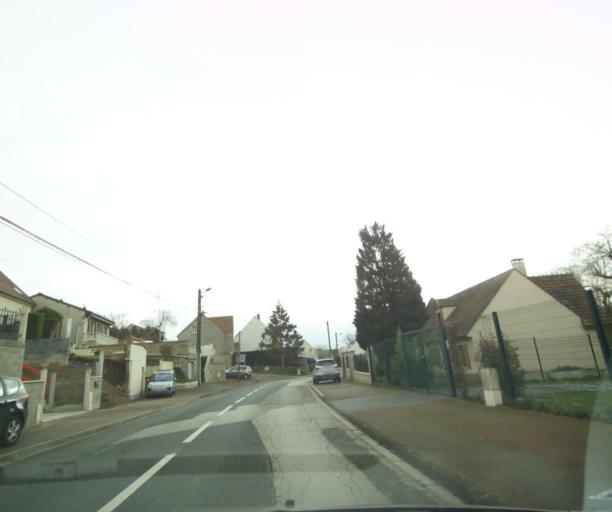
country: FR
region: Picardie
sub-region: Departement de l'Oise
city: Noyon
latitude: 49.5884
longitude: 2.9938
